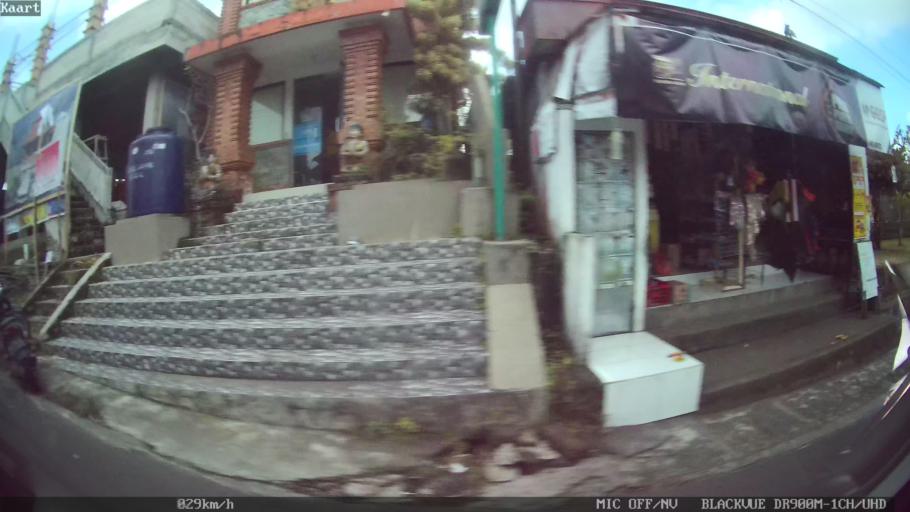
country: ID
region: Bali
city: Banjar Petak
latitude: -8.4466
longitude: 115.3191
